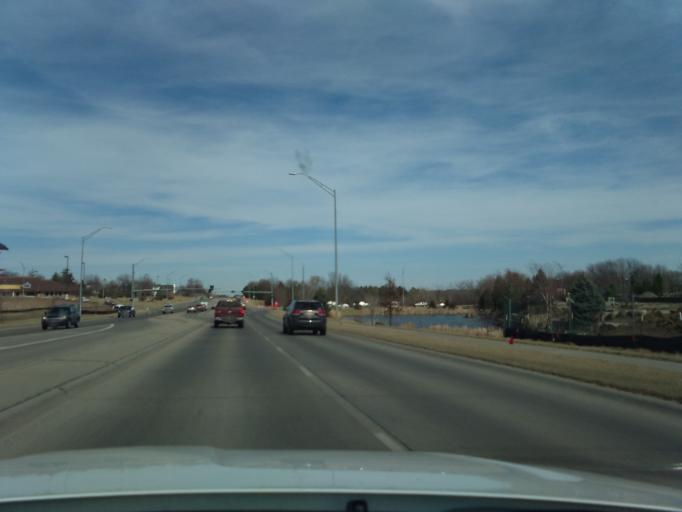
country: US
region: Nebraska
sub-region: Lancaster County
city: Lincoln
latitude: 40.7390
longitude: -96.6443
